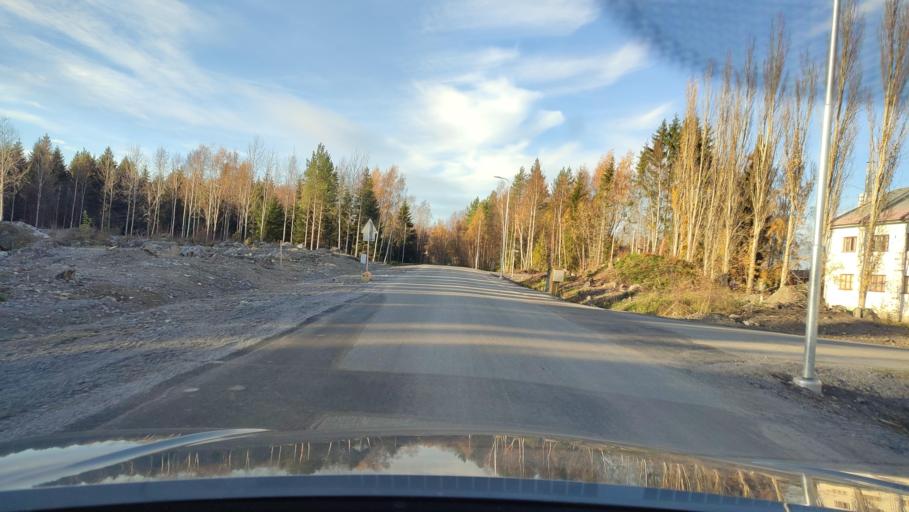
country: FI
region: Ostrobothnia
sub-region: Vaasa
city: Teeriniemi
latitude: 63.0655
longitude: 21.6997
